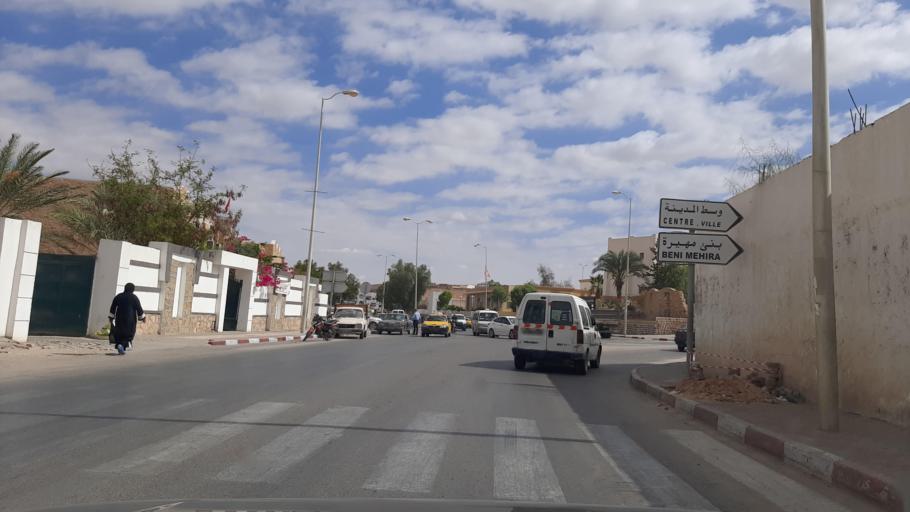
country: TN
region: Tataouine
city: Tataouine
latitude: 32.9266
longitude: 10.4429
